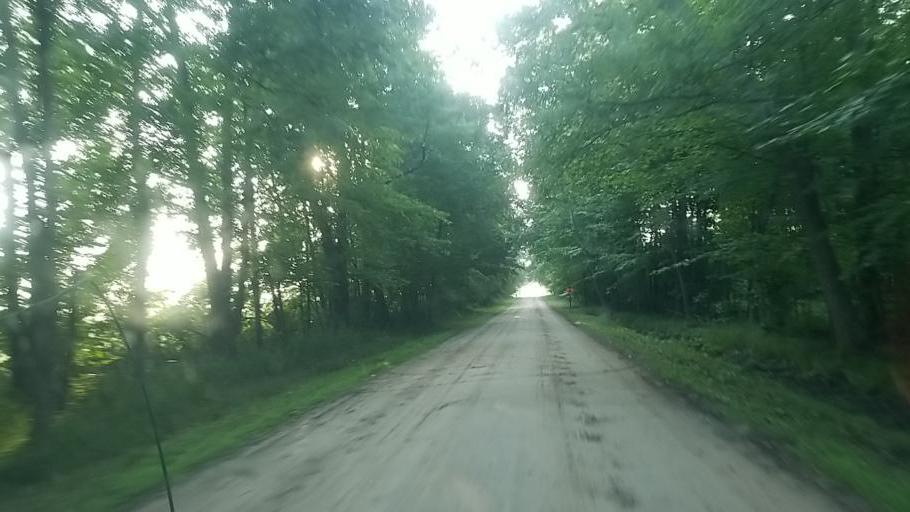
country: US
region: Michigan
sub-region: Muskegon County
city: Twin Lake
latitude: 43.4533
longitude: -86.0832
